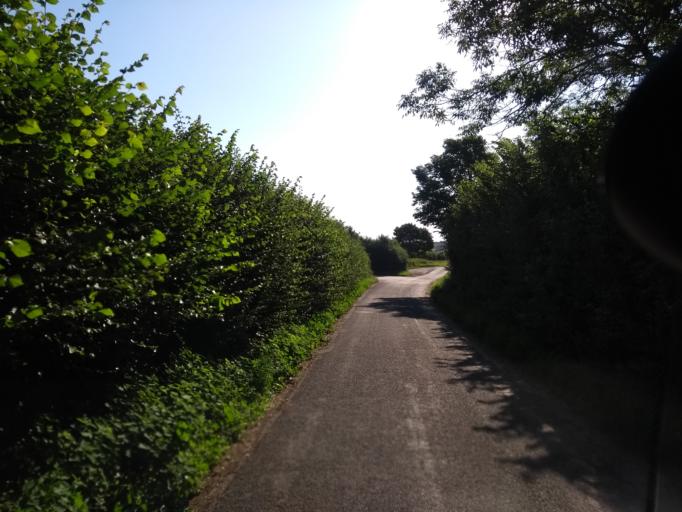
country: GB
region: England
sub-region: Somerset
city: Westonzoyland
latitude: 51.1399
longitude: -2.8993
